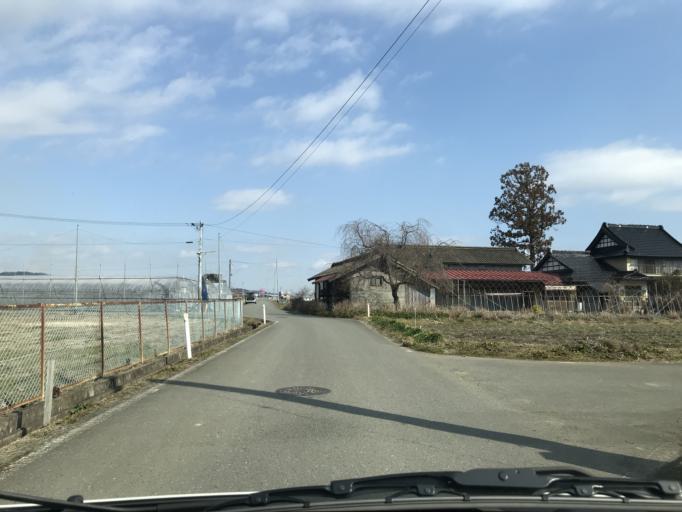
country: JP
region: Iwate
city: Mizusawa
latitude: 39.0380
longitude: 141.1280
